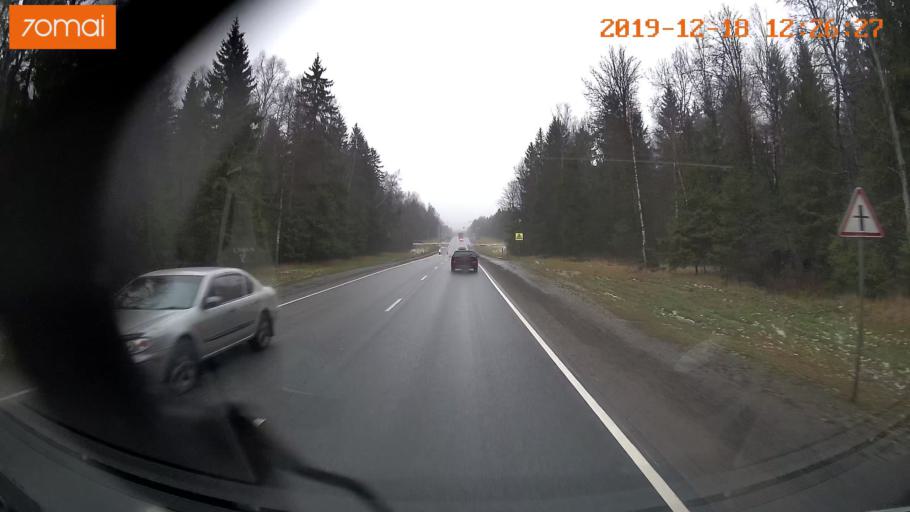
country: RU
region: Moskovskaya
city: Novopetrovskoye
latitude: 56.0513
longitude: 36.5011
